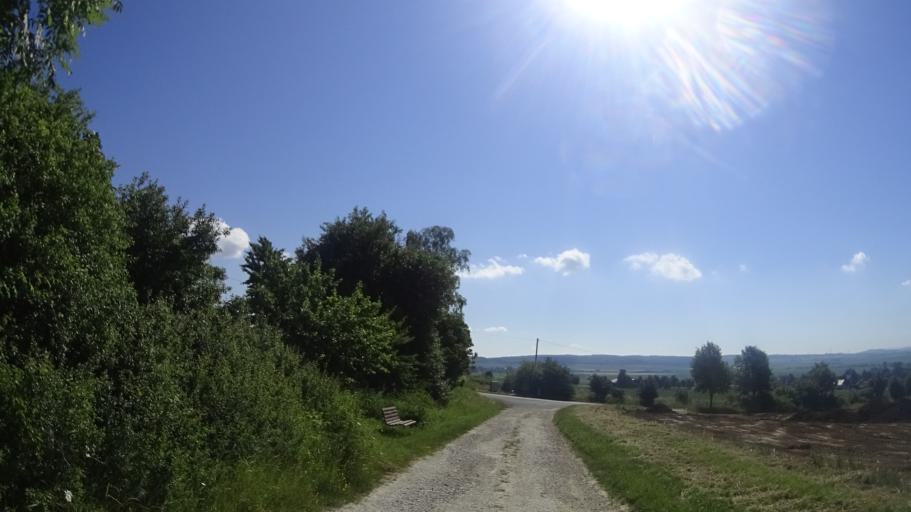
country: DE
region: Lower Saxony
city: Elbe
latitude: 52.0956
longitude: 10.2623
